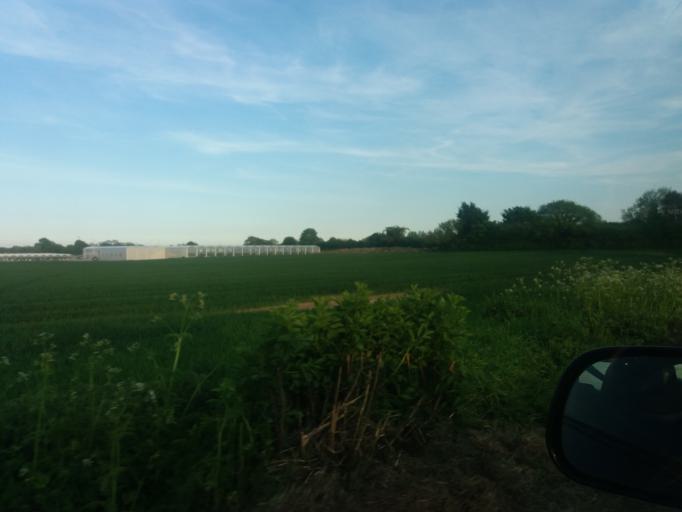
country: IE
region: Leinster
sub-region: Fingal County
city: Swords
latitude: 53.4849
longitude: -6.2259
